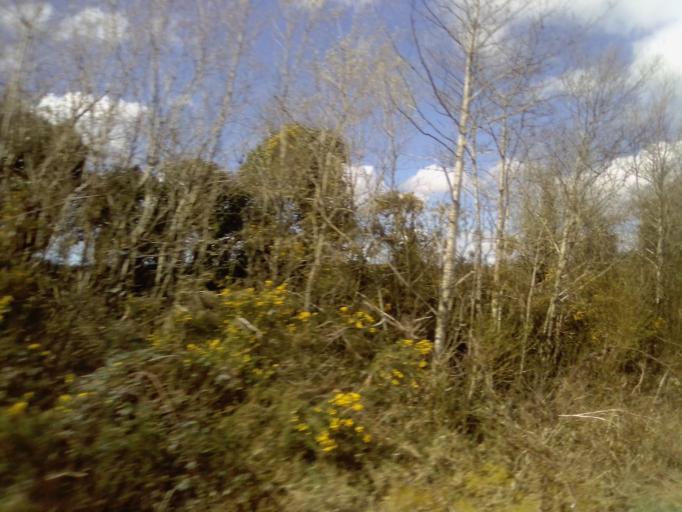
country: IE
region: Munster
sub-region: Ciarrai
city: Cill Airne
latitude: 52.0670
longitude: -9.3052
